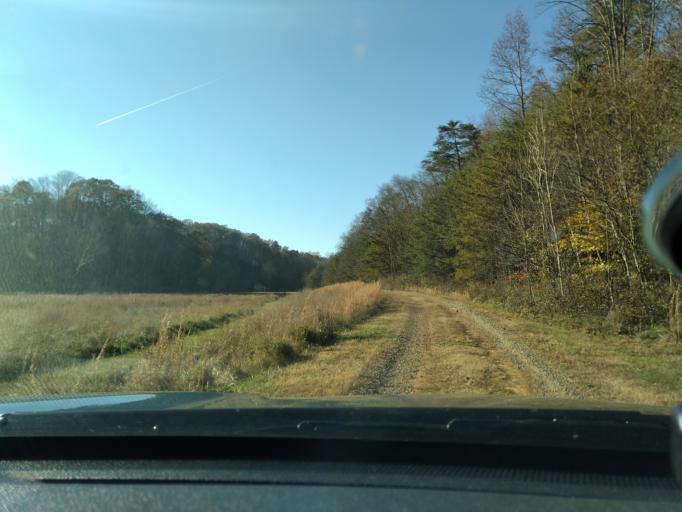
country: US
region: Virginia
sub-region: Floyd County
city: Floyd
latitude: 36.8341
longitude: -80.1806
